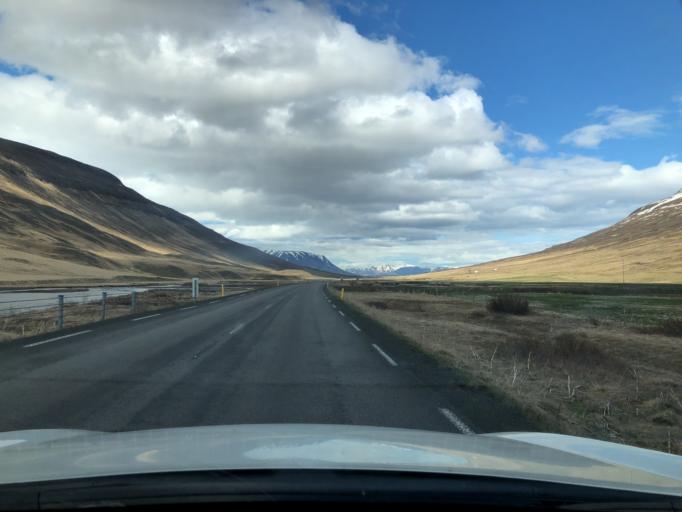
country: IS
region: Northeast
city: Dalvik
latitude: 65.6290
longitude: -18.4824
